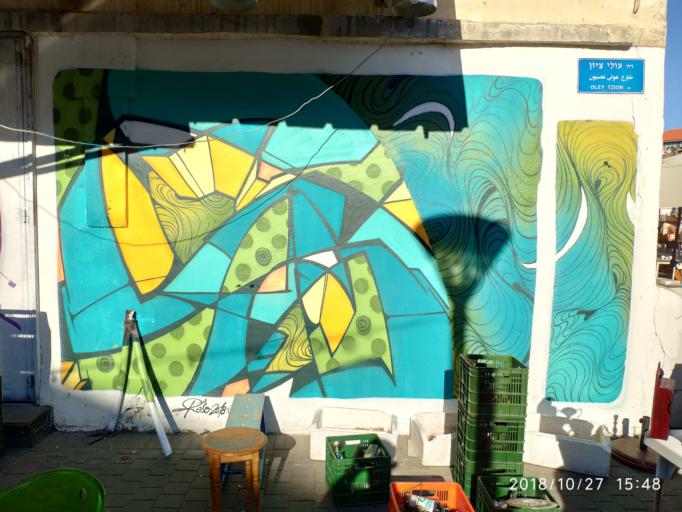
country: IL
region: Tel Aviv
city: Yafo
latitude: 32.0531
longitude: 34.7567
